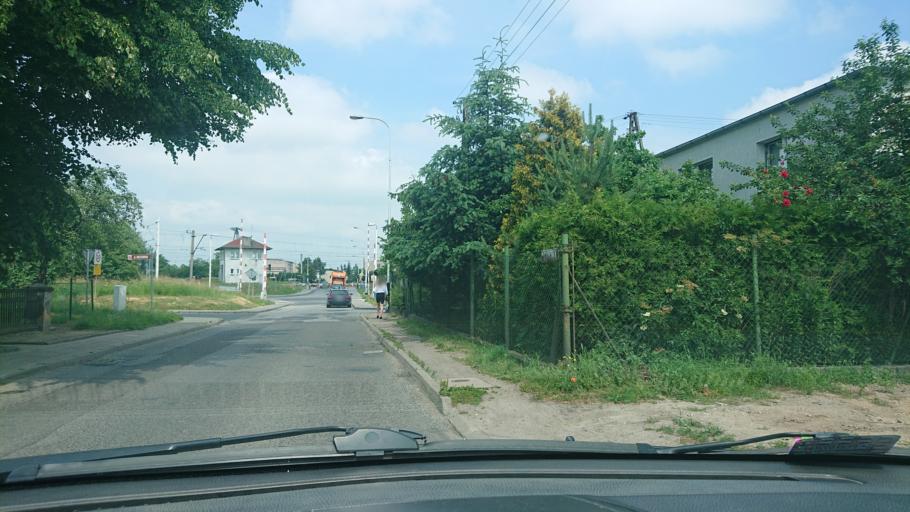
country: PL
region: Greater Poland Voivodeship
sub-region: Powiat gnieznienski
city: Gniezno
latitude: 52.5251
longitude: 17.5814
